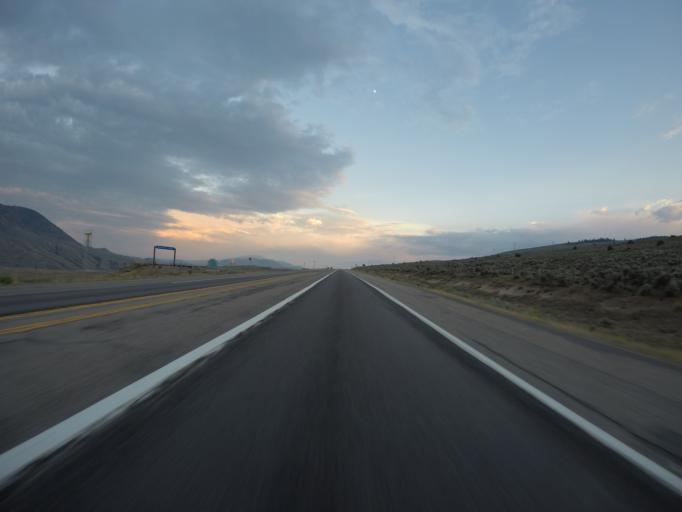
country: US
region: Colorado
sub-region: Grand County
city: Kremmling
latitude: 40.1147
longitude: -106.4284
